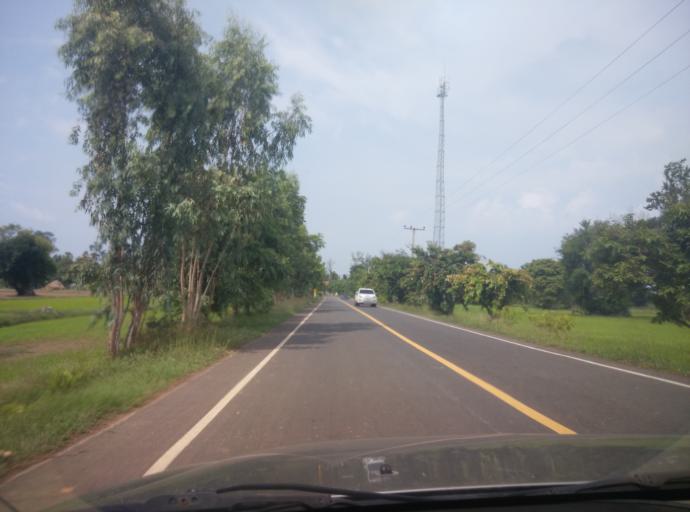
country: TH
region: Sisaket
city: Huai Thap Than
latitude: 15.0327
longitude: 104.0761
